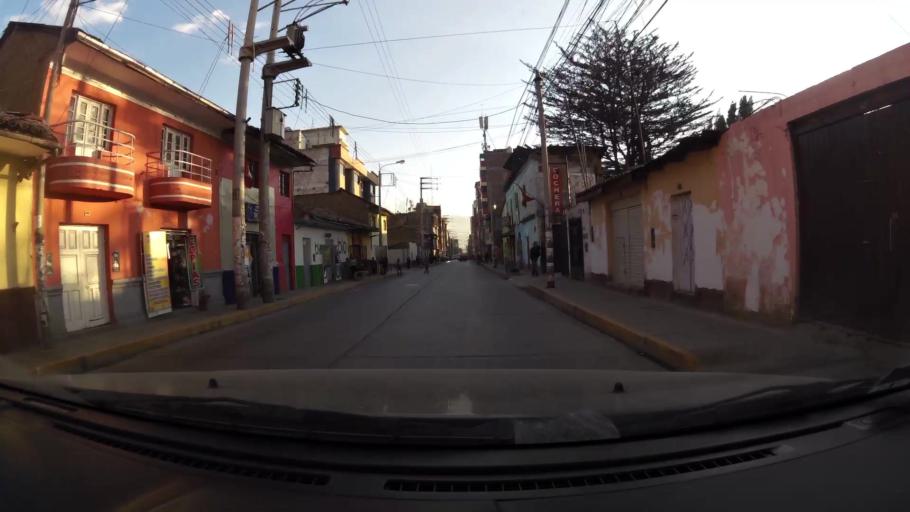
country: PE
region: Junin
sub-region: Provincia de Huancayo
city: Huancayo
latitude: -12.0644
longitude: -75.2083
